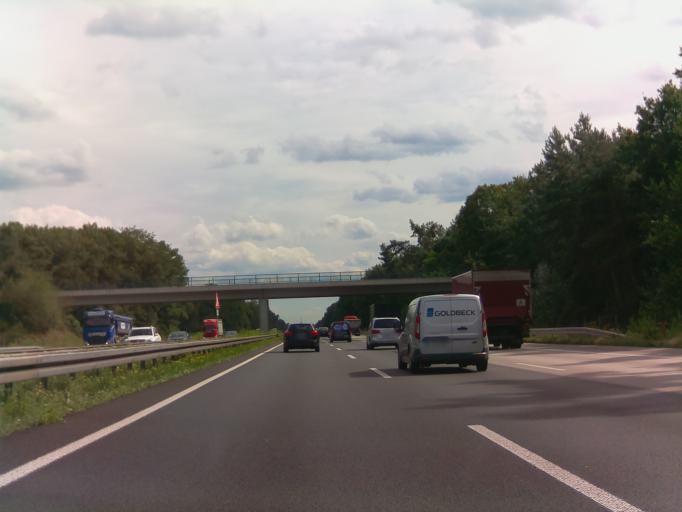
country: DE
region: Hesse
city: Lorsch
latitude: 49.6292
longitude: 8.5550
